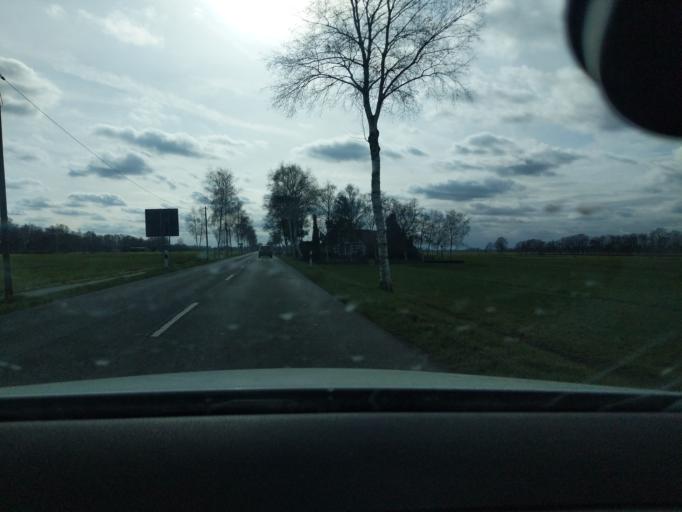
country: DE
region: Lower Saxony
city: Drochtersen
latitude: 53.6675
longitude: 9.3828
